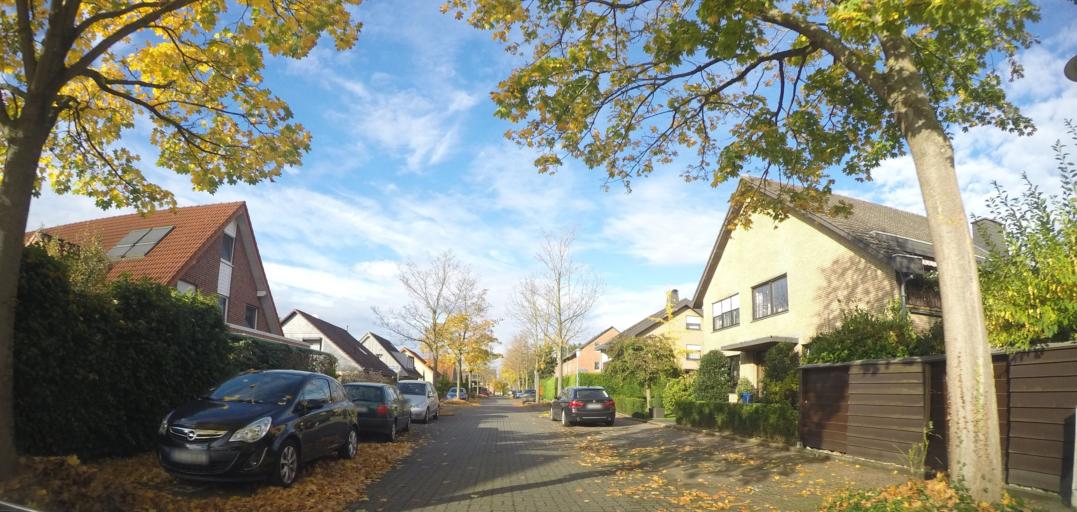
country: DE
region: North Rhine-Westphalia
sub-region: Regierungsbezirk Arnsberg
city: Lippstadt
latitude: 51.6581
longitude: 8.3272
